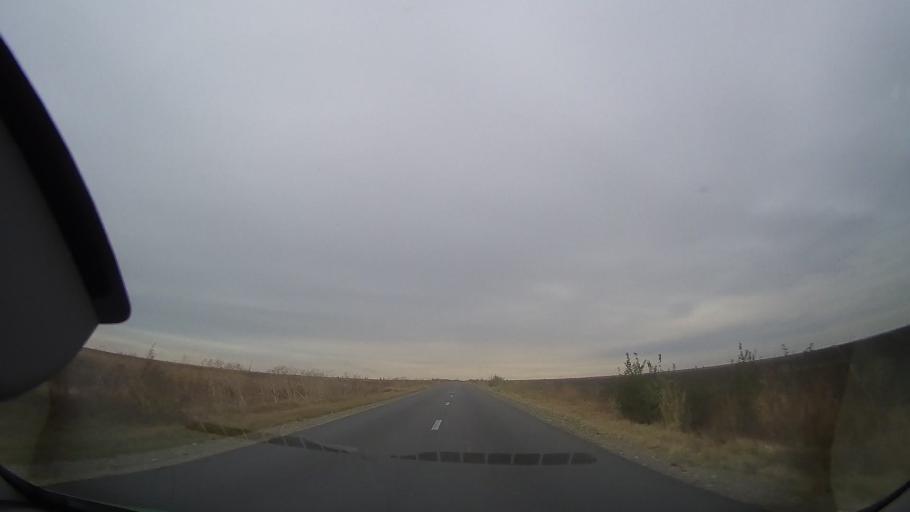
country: RO
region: Ialomita
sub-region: Oras Amara
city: Amara
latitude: 44.6419
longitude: 27.3006
